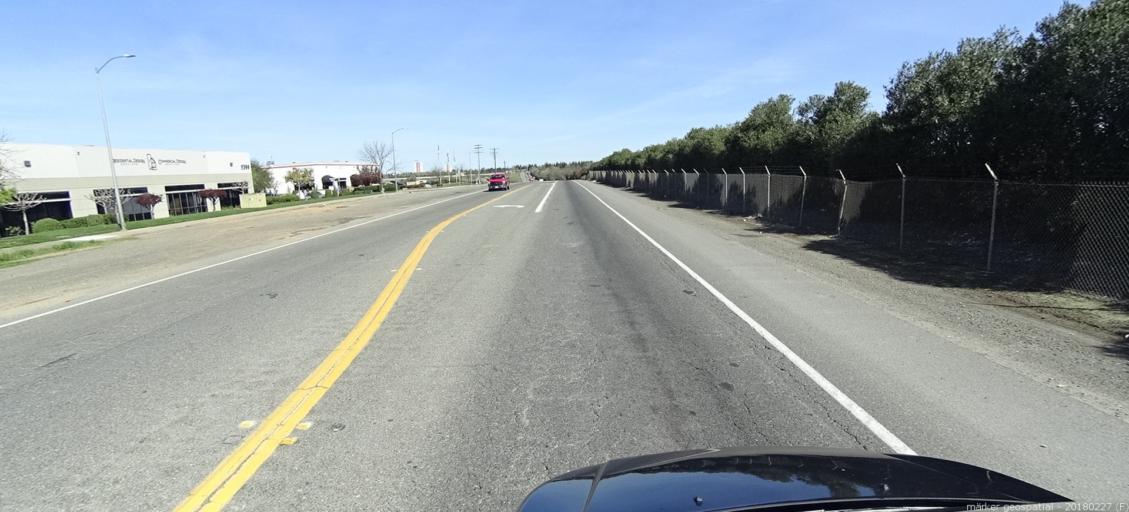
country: US
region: California
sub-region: Sacramento County
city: Rosemont
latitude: 38.5273
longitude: -121.3702
